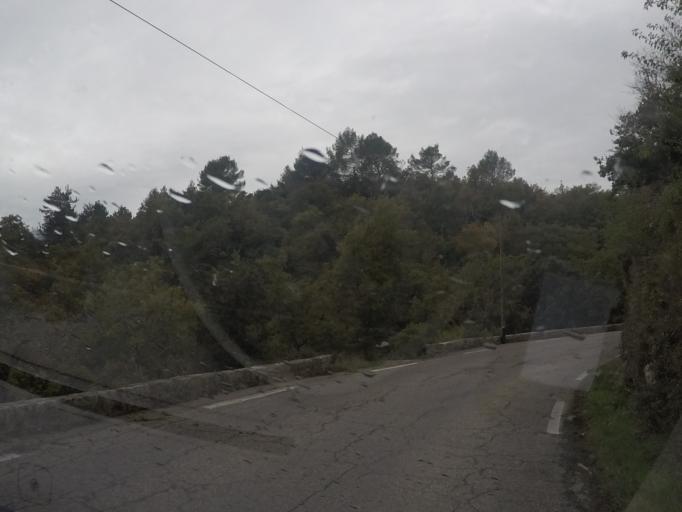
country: FR
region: Provence-Alpes-Cote d'Azur
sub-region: Departement du Vaucluse
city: Bonnieux
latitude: 43.8138
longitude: 5.3328
